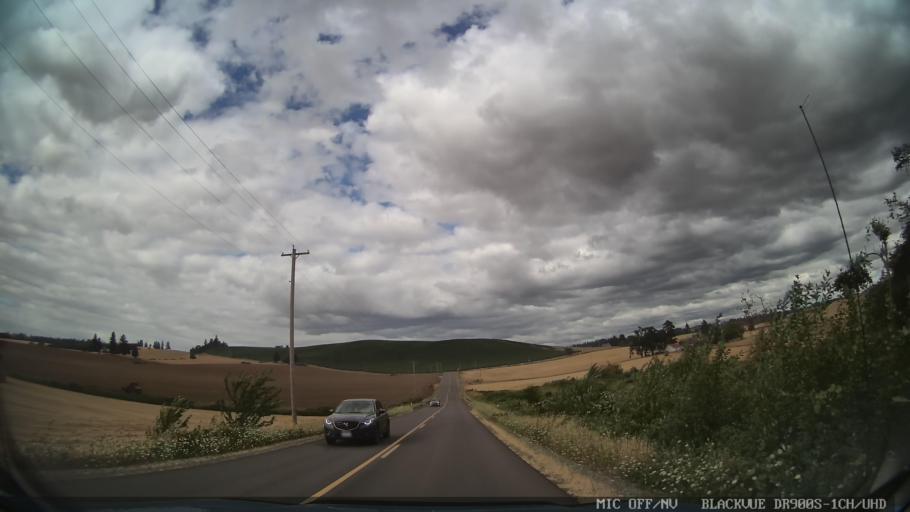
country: US
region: Oregon
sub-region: Marion County
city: Sublimity
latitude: 44.8693
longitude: -122.7377
